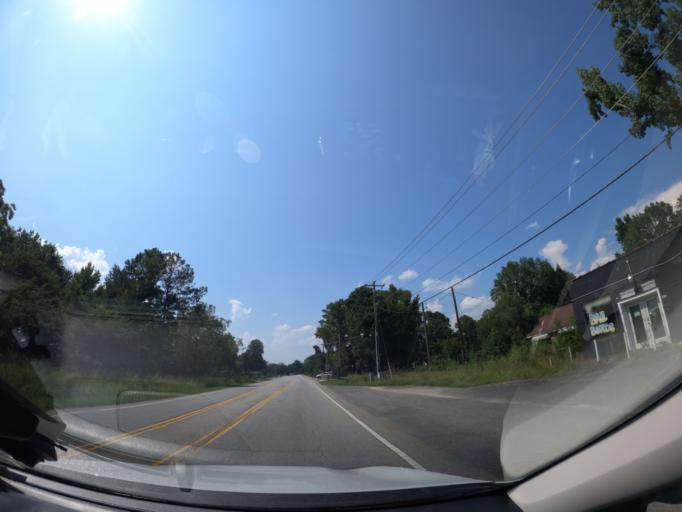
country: US
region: South Carolina
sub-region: Richland County
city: Forest Acres
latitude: 33.9317
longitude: -80.9686
